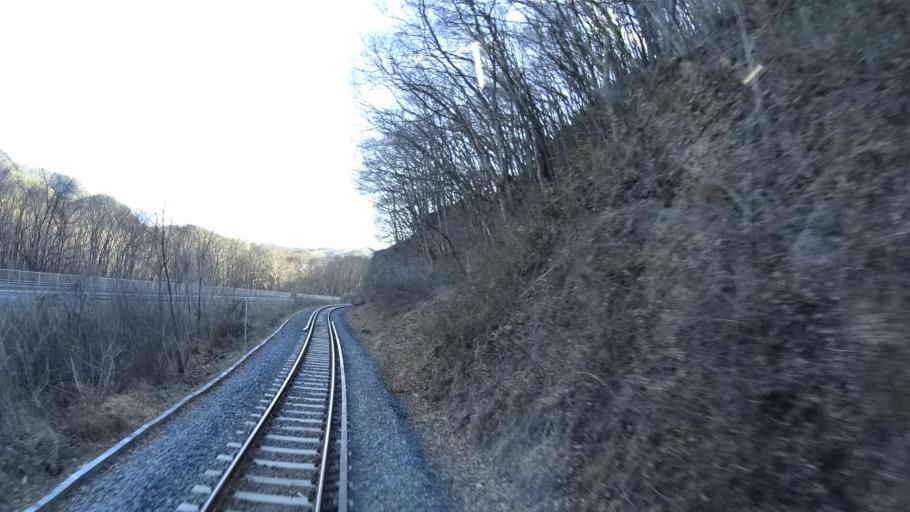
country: JP
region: Iwate
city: Yamada
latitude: 39.5530
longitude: 141.9398
